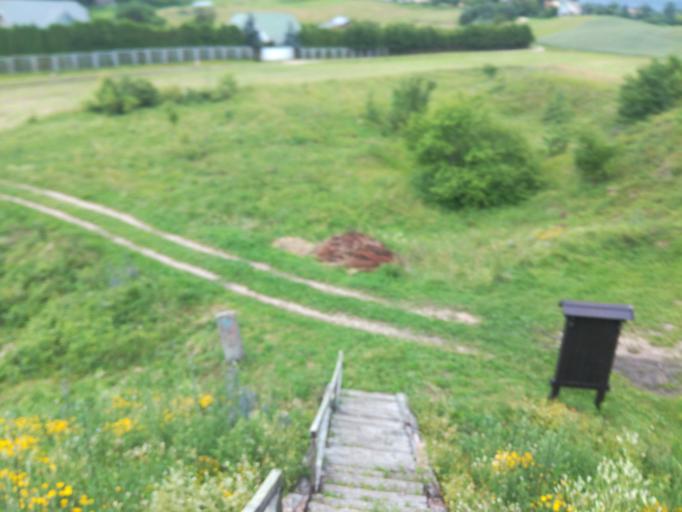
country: LT
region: Alytaus apskritis
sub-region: Alytus
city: Alytus
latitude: 54.4726
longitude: 24.0515
